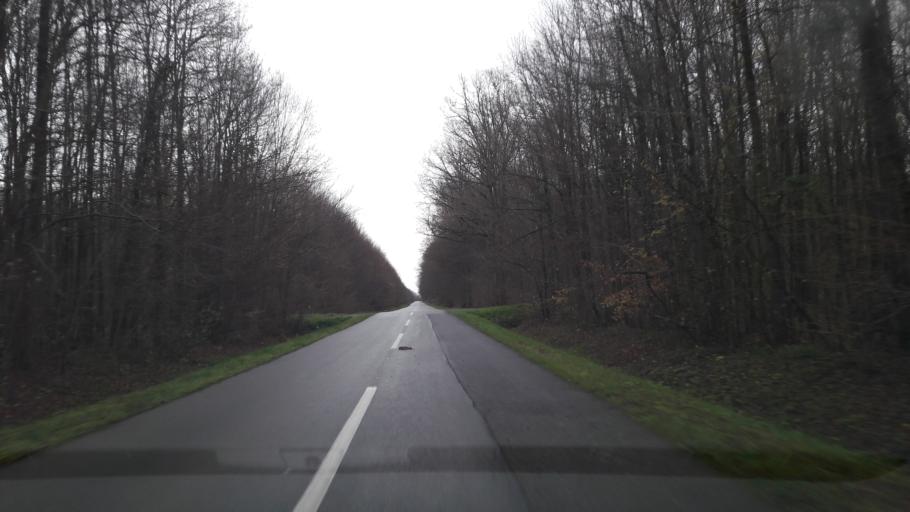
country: HR
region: Osjecko-Baranjska
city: Velimirovac
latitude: 45.6297
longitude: 18.0923
